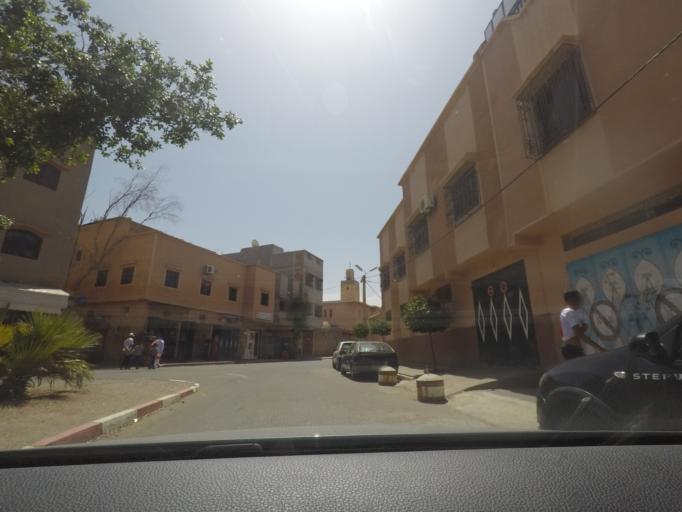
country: MA
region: Marrakech-Tensift-Al Haouz
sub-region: Marrakech
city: Marrakesh
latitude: 31.5940
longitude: -8.0275
